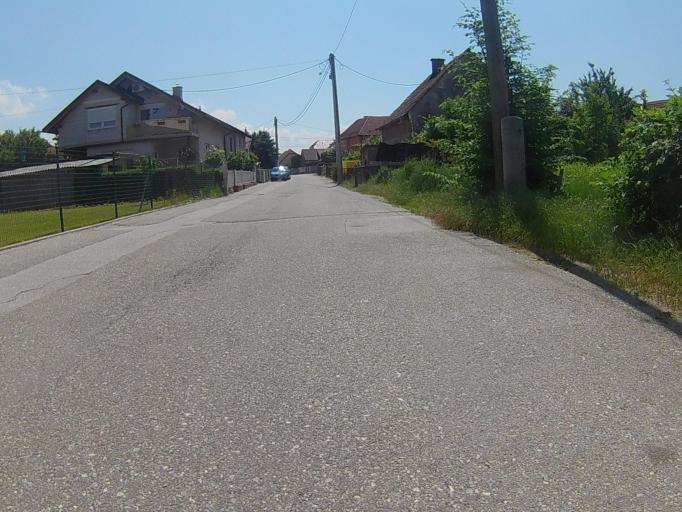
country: SI
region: Hoce-Slivnica
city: Rogoza
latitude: 46.5316
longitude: 15.6752
